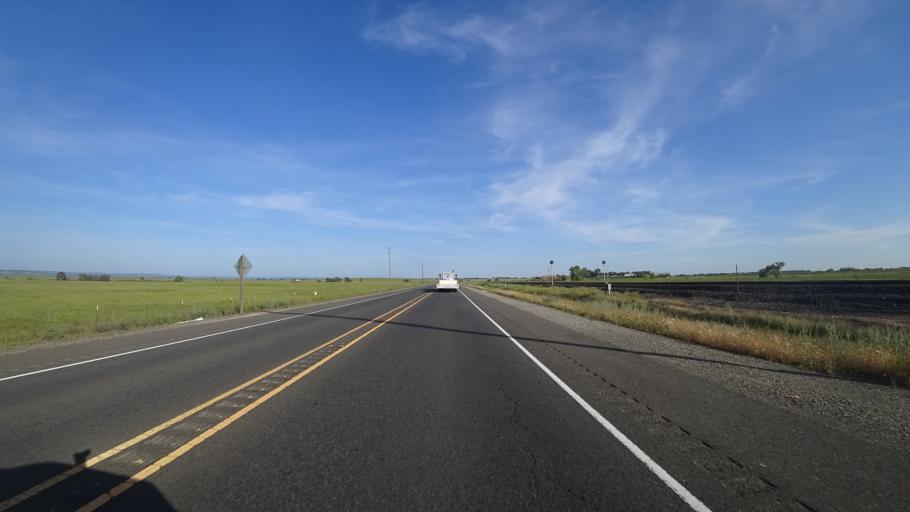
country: US
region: California
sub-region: Placer County
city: Sheridan
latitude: 38.9616
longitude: -121.3601
